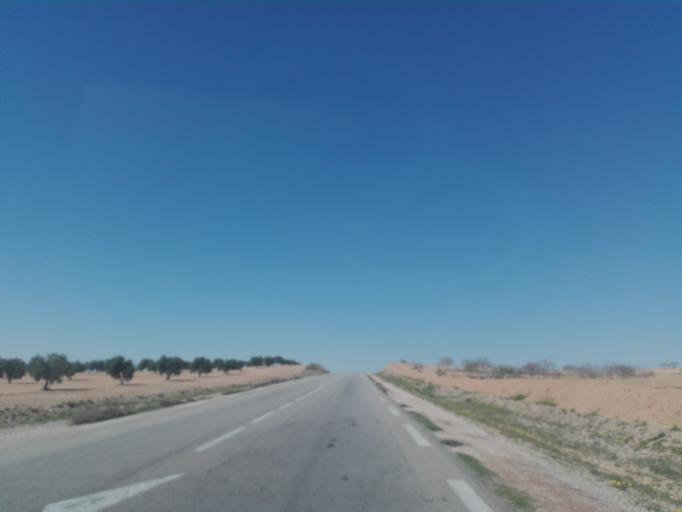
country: TN
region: Safaqis
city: Bi'r `Ali Bin Khalifah
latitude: 34.7579
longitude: 10.2813
